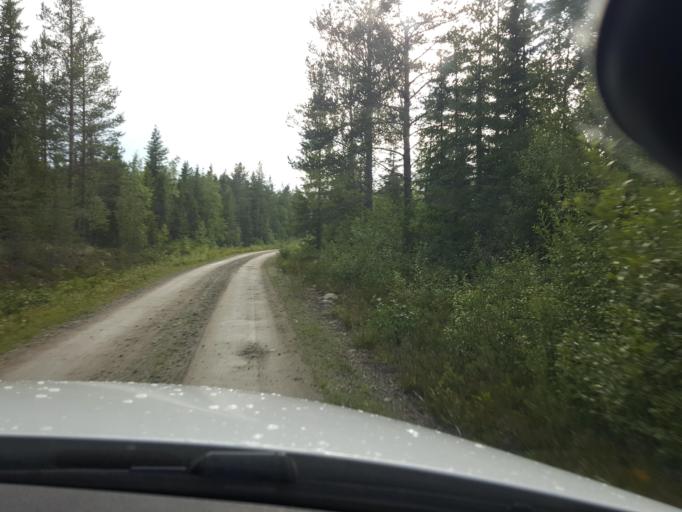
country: SE
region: Vaesternorrland
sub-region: Ange Kommun
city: Fransta
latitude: 62.2040
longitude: 16.1449
